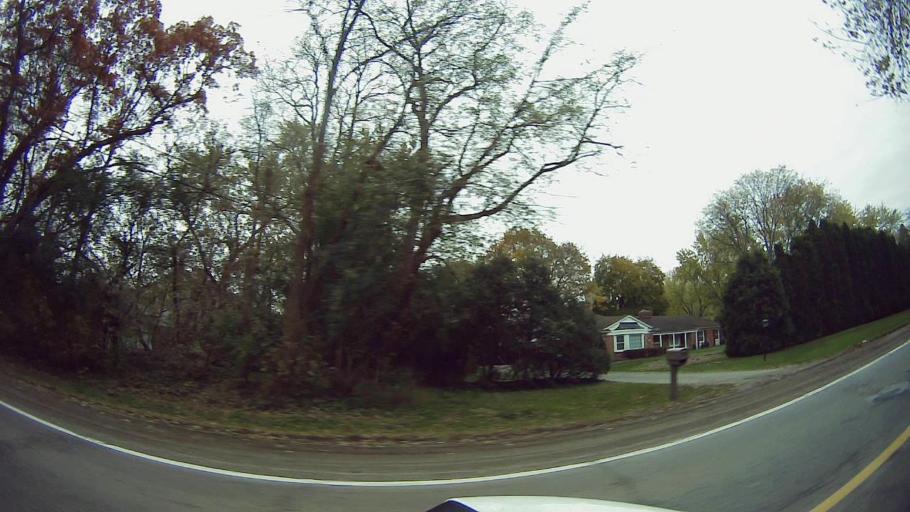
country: US
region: Michigan
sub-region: Oakland County
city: Franklin
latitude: 42.5153
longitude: -83.2973
